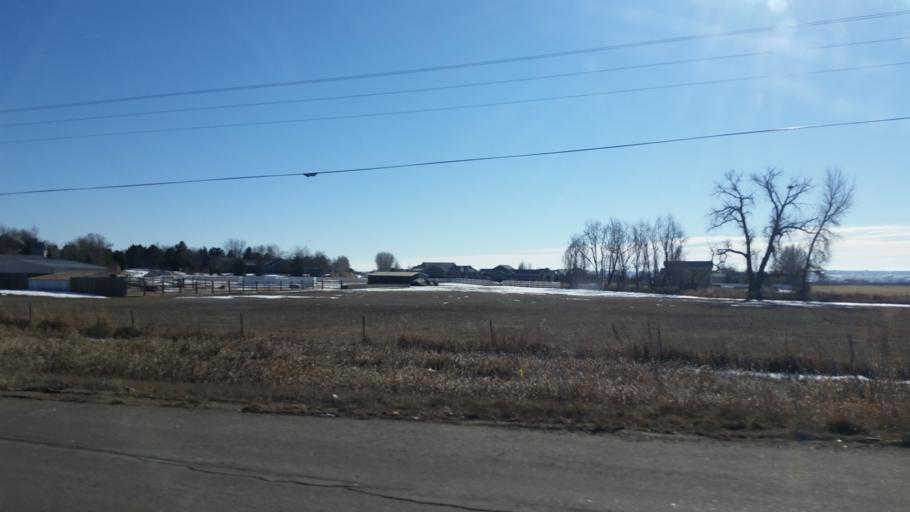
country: US
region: Colorado
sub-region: Weld County
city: Johnstown
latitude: 40.4066
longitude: -104.9358
